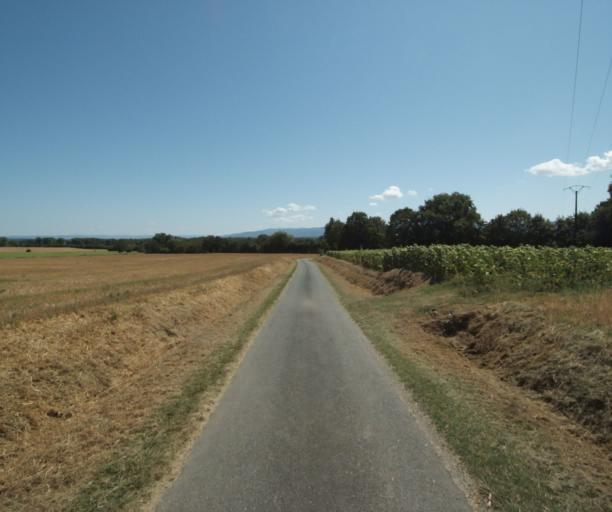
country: FR
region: Midi-Pyrenees
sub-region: Departement de la Haute-Garonne
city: Revel
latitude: 43.4955
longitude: 1.9459
